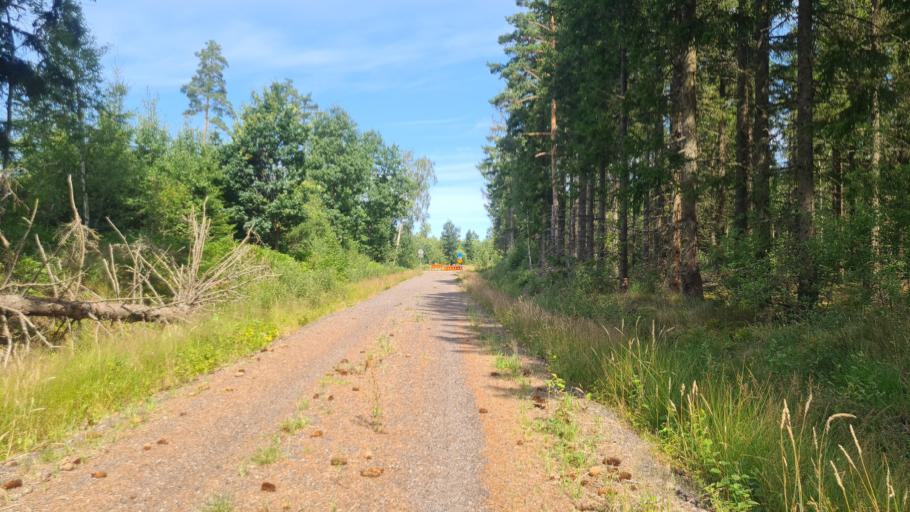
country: SE
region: Kronoberg
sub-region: Ljungby Kommun
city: Lagan
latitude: 56.9833
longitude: 13.9449
